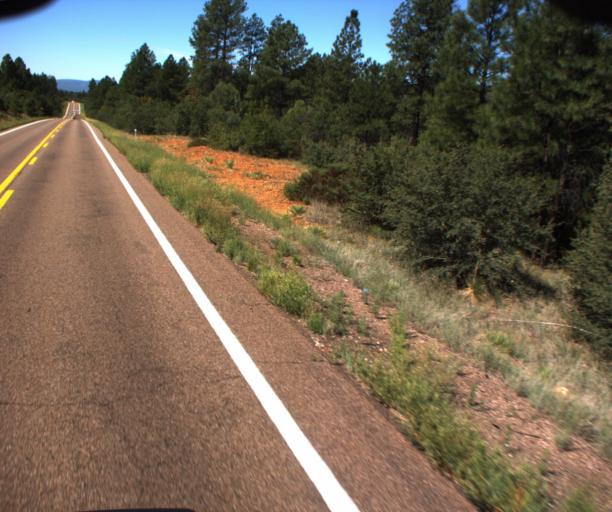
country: US
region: Arizona
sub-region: Navajo County
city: Linden
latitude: 34.0808
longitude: -110.1878
